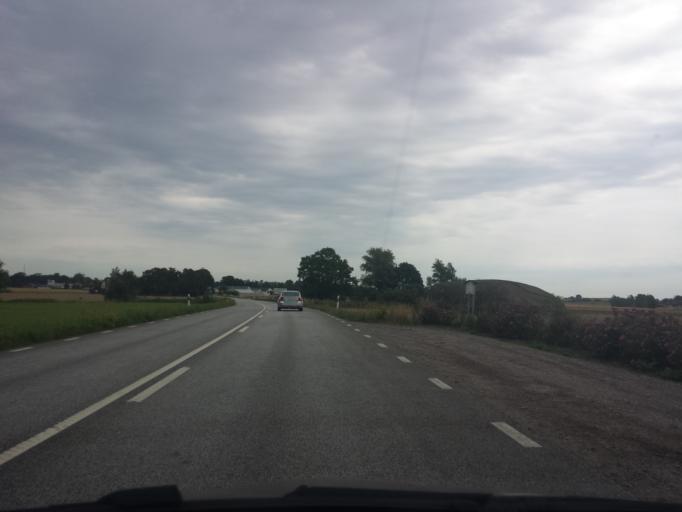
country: SE
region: Skane
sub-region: Ystads Kommun
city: Kopingebro
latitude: 55.4439
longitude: 14.0098
